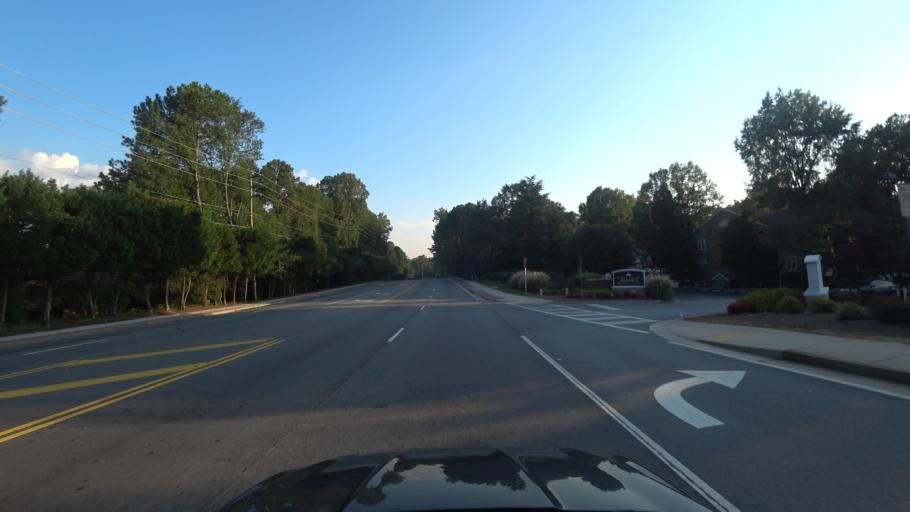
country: US
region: Georgia
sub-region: DeKalb County
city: North Atlanta
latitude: 33.8541
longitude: -84.3138
